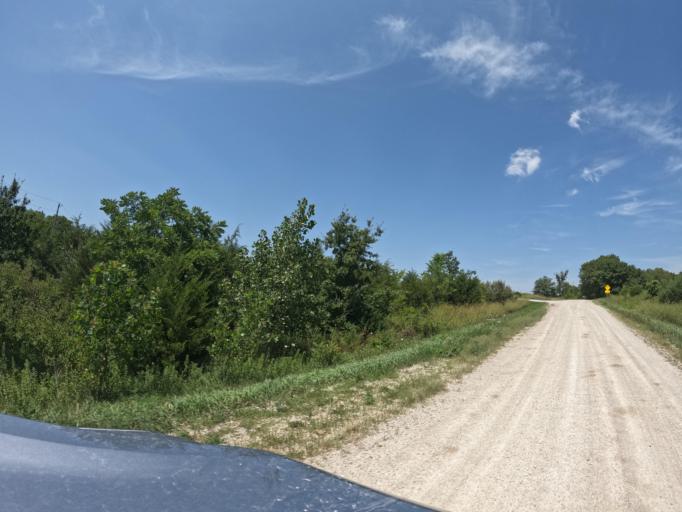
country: US
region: Iowa
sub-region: Henry County
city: Mount Pleasant
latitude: 40.9189
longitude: -91.6652
